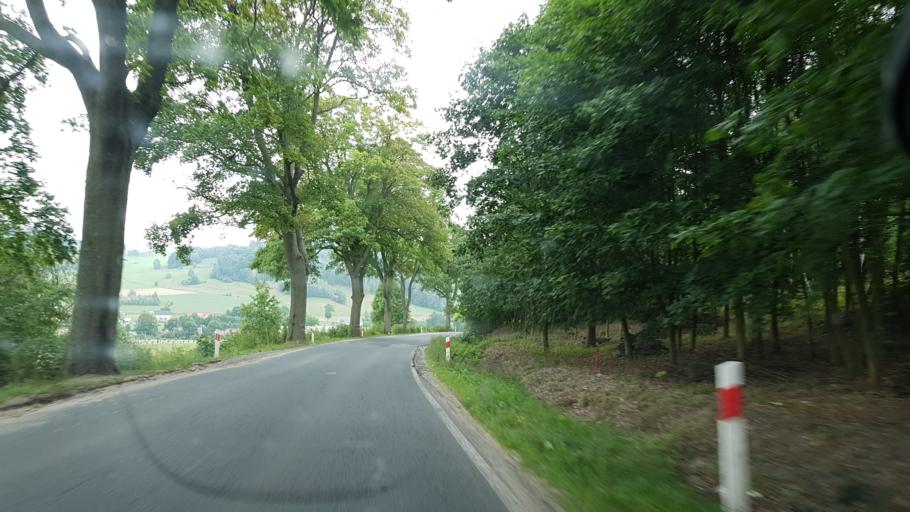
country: PL
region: Lower Silesian Voivodeship
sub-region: Powiat kamiennogorski
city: Marciszow
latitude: 50.8935
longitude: 15.9897
